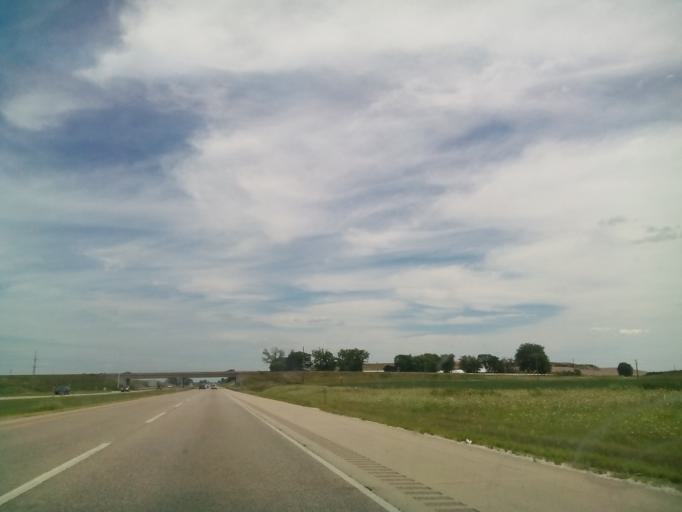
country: US
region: Illinois
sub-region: DeKalb County
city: Cortland
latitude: 41.9006
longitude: -88.6928
